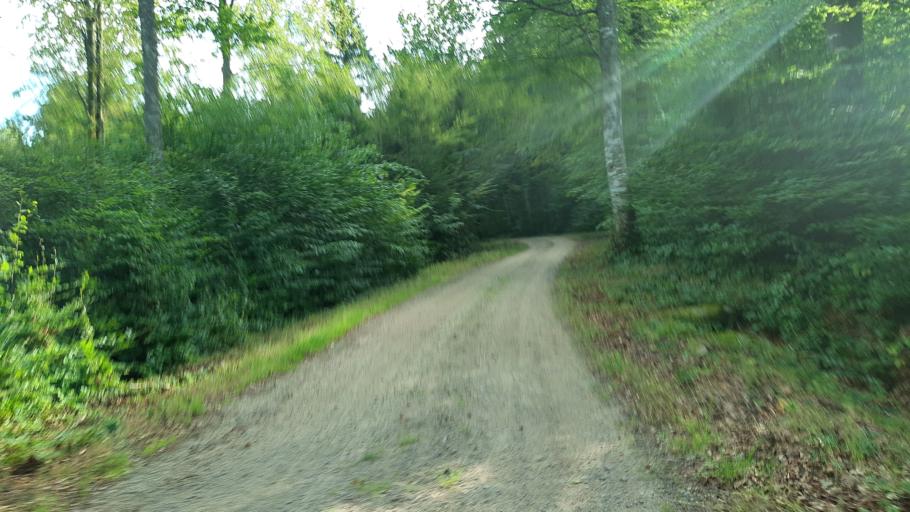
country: SE
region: Blekinge
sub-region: Ronneby Kommun
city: Kallinge
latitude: 56.2422
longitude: 15.3969
